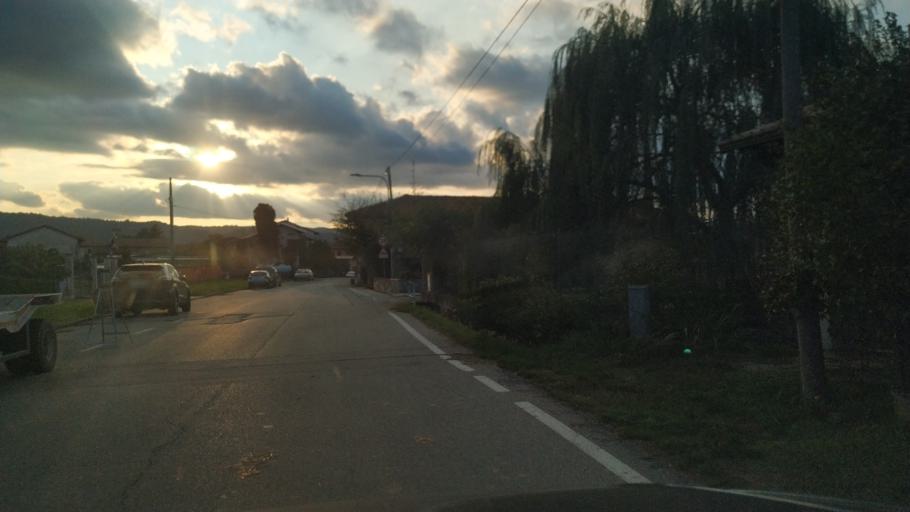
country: IT
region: Piedmont
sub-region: Provincia di Biella
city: Vergnasco
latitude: 45.4740
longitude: 8.0889
